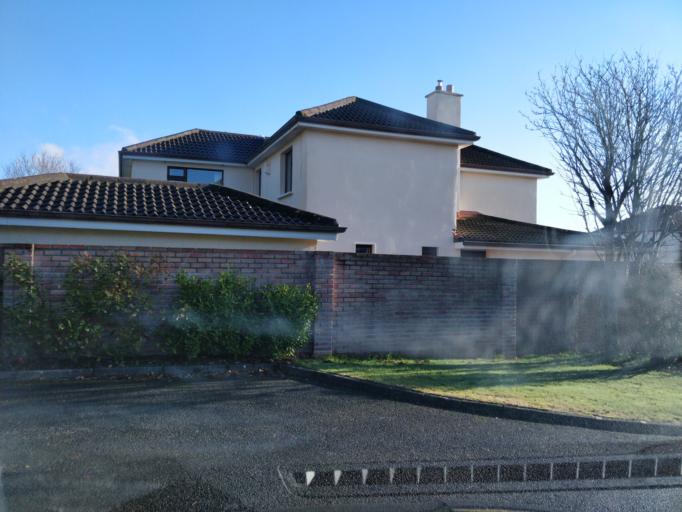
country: IE
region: Connaught
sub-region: County Galway
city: Bearna
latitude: 53.2619
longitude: -9.1193
